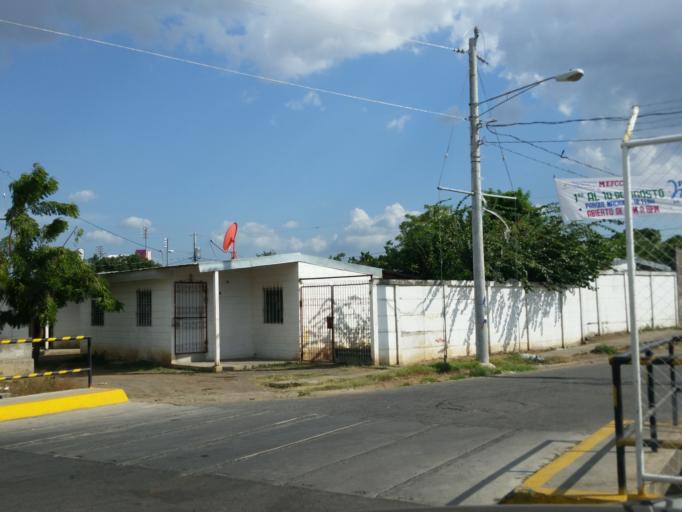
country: NI
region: Managua
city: Managua
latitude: 12.1614
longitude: -86.2758
